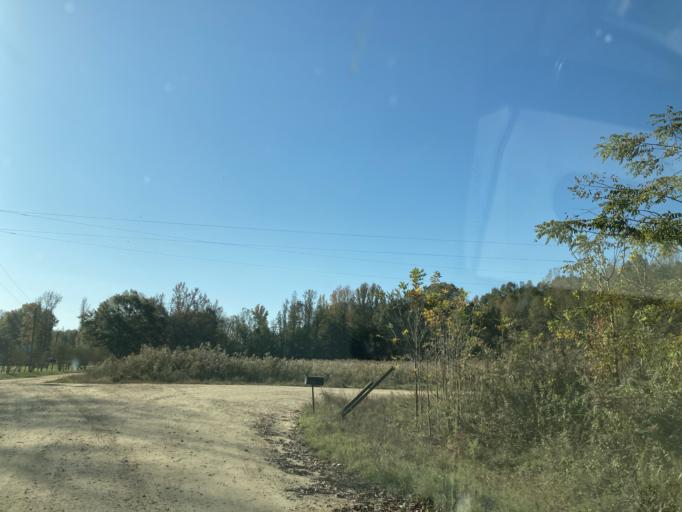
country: US
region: Mississippi
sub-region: Madison County
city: Kearney Park
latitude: 32.7351
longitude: -90.3063
